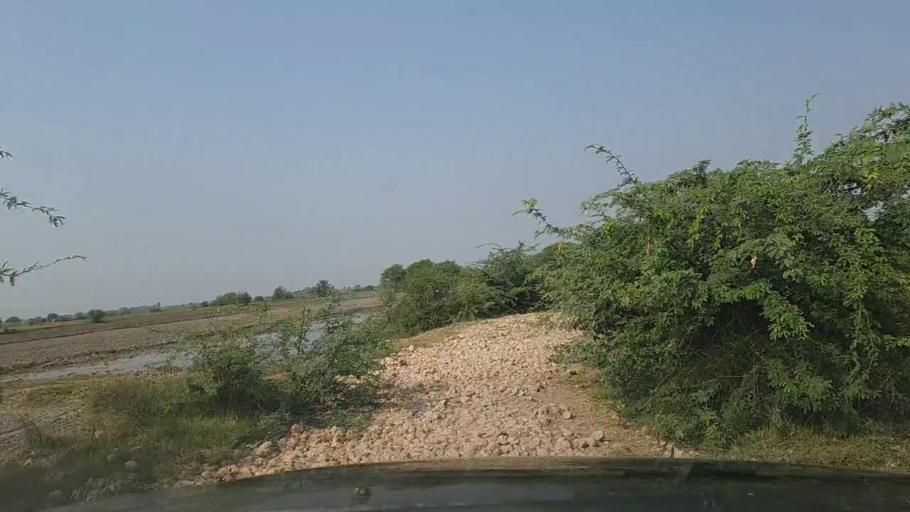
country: PK
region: Sindh
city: Mirpur Batoro
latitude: 24.6851
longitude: 68.2362
